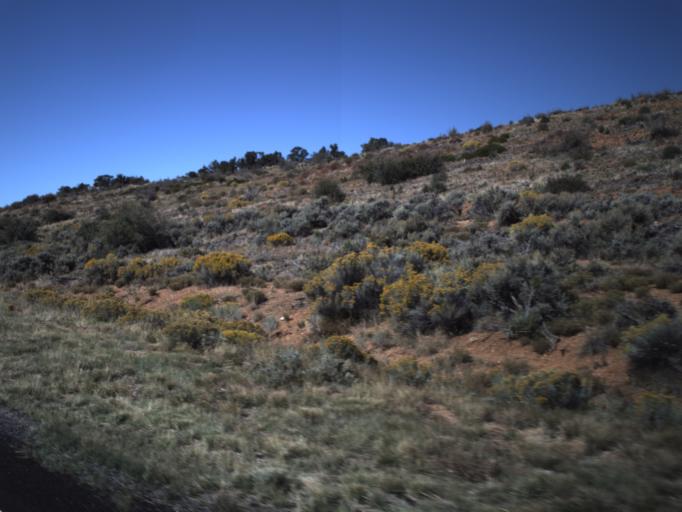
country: US
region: Utah
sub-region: Iron County
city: Cedar City
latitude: 37.6128
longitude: -113.3437
